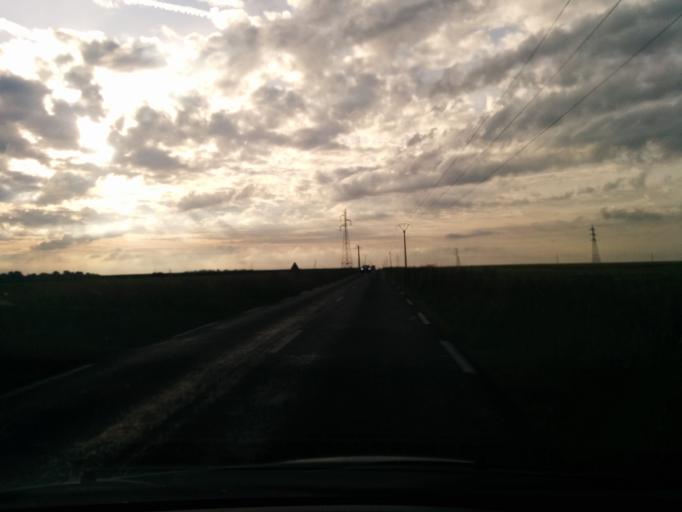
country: FR
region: Ile-de-France
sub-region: Departement des Yvelines
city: Limetz-Villez
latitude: 49.0955
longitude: 1.5273
